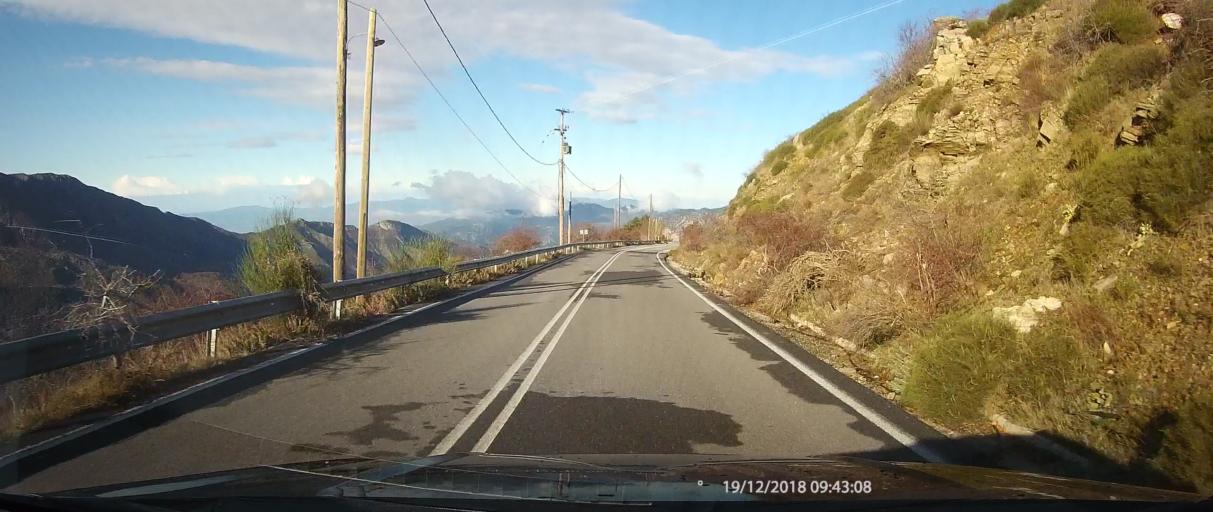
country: GR
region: Peloponnese
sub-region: Nomos Messinias
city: Paralia Vergas
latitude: 37.0705
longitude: 22.2593
